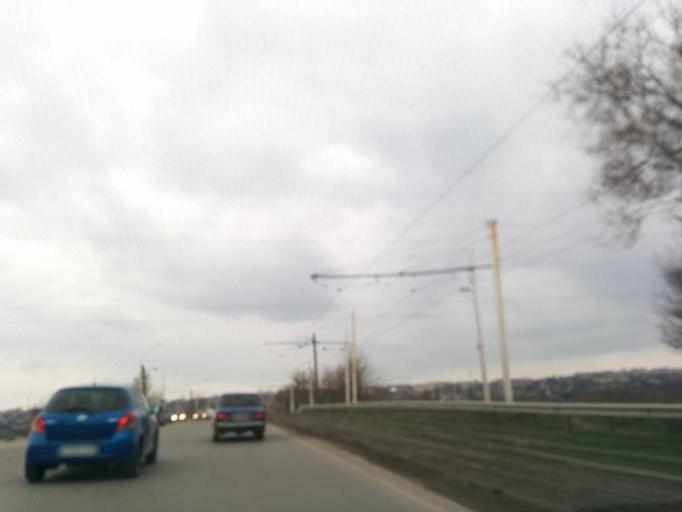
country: RU
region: Rostov
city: Novocherkassk
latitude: 47.4365
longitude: 40.0995
